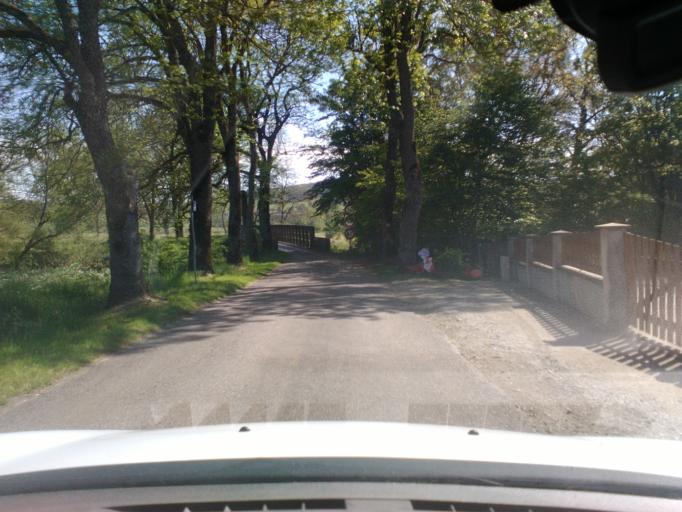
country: FR
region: Lorraine
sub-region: Departement des Vosges
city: Mirecourt
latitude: 48.3246
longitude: 6.1446
